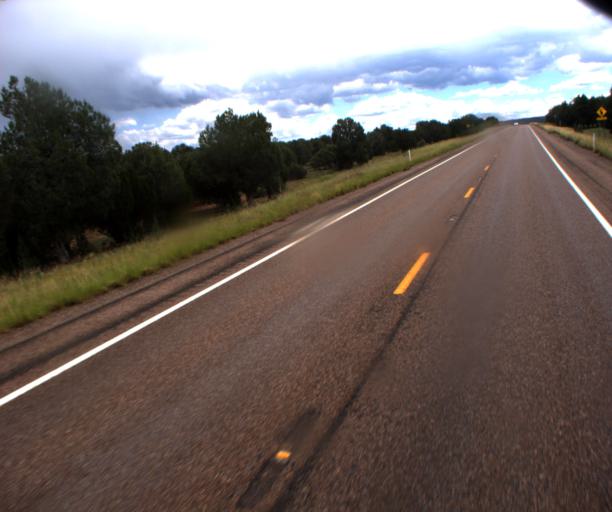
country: US
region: Arizona
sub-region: Navajo County
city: Linden
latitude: 34.3602
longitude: -110.3230
